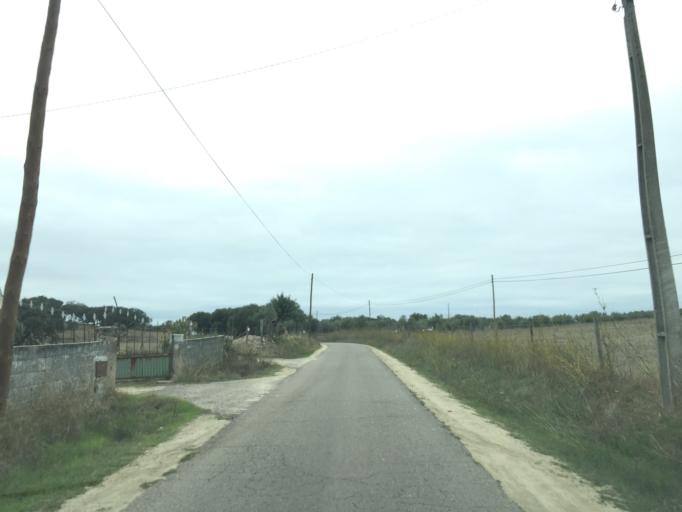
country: PT
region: Portalegre
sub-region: Fronteira
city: Vale da Amoreira
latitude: 39.0508
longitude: -7.7706
